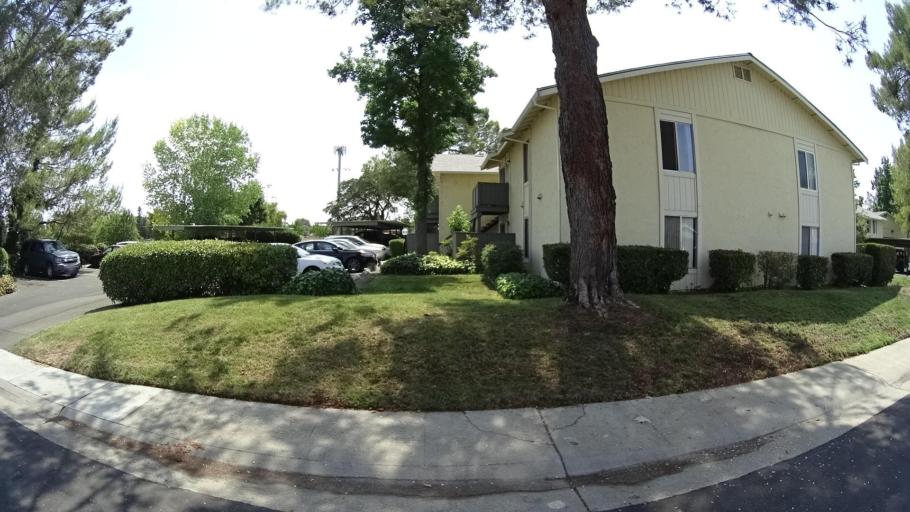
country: US
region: California
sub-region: Placer County
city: Rocklin
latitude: 38.7874
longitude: -121.2482
